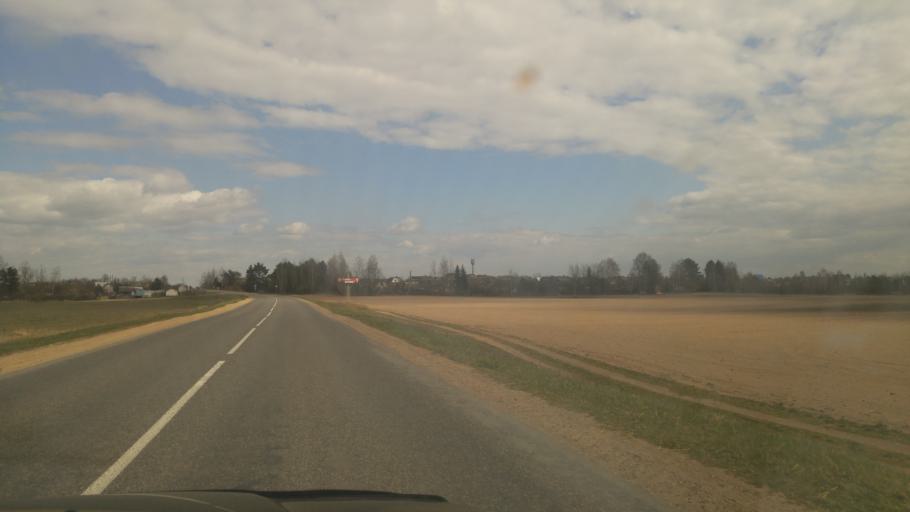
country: BY
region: Minsk
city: Rudzyensk
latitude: 53.6556
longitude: 27.8188
